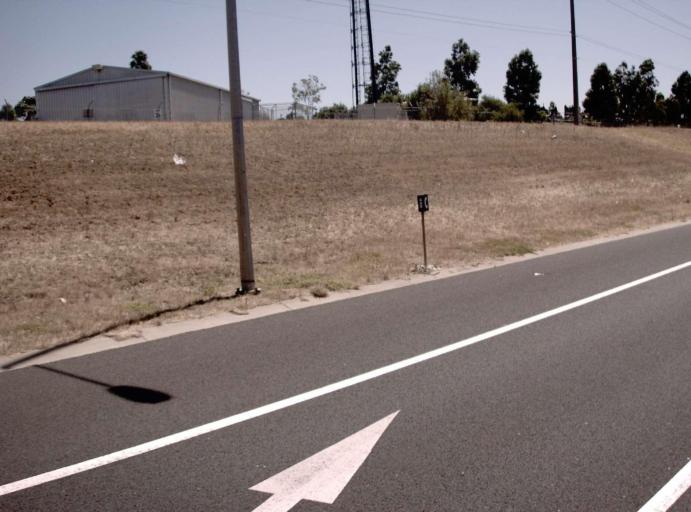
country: AU
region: Victoria
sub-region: Moonee Valley
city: Keilor East
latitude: -37.7314
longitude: 144.8549
